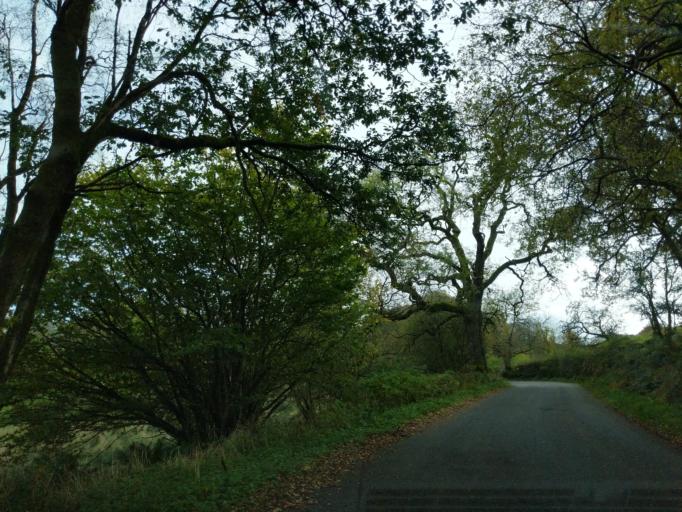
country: GB
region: Scotland
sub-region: Dumfries and Galloway
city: Castle Douglas
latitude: 55.1071
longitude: -4.1246
